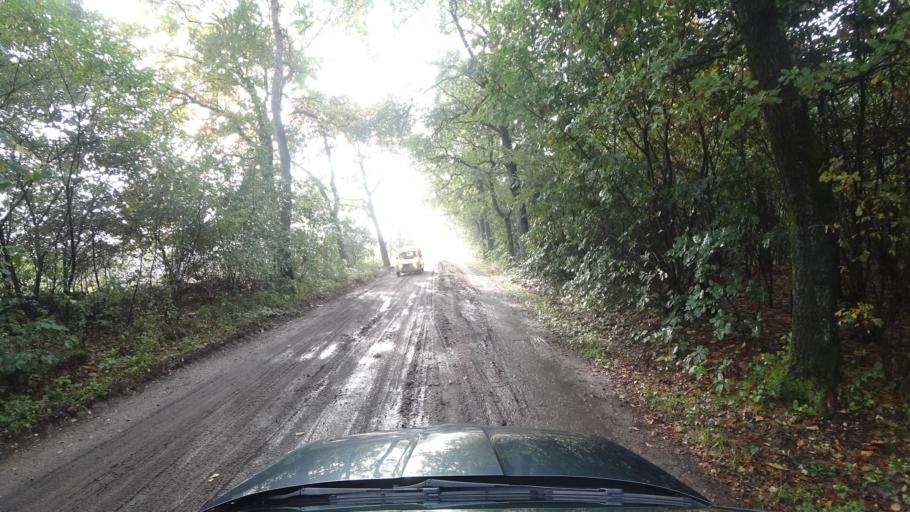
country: NL
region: Gelderland
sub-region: Gemeente Renkum
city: Renkum
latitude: 51.9933
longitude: 5.7384
